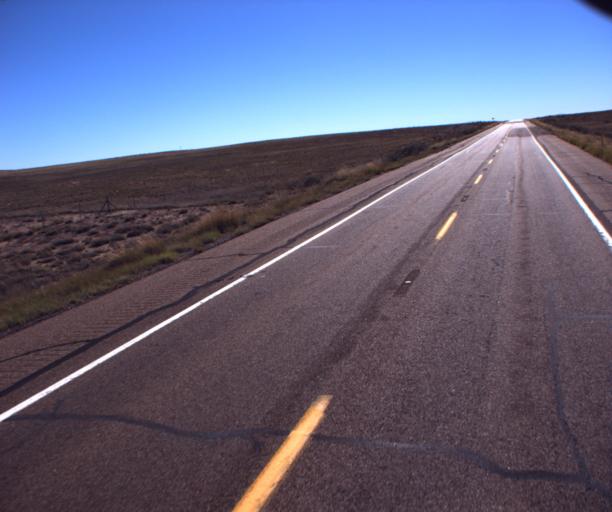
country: US
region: Arizona
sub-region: Navajo County
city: Holbrook
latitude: 34.8163
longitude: -109.9230
